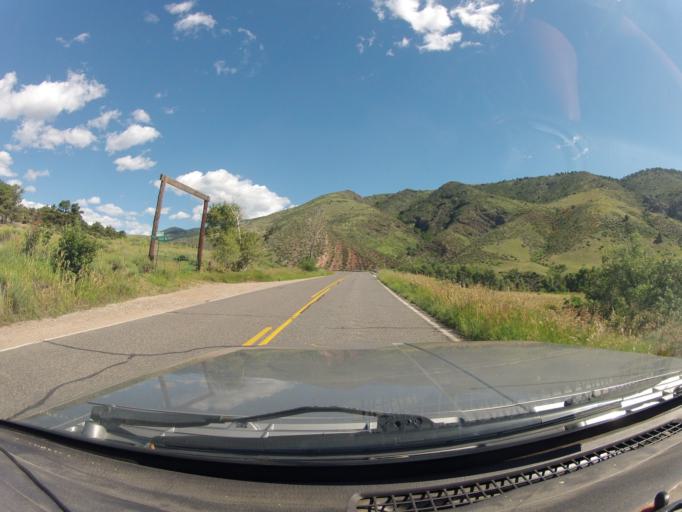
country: US
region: Colorado
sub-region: Larimer County
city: Laporte
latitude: 40.5072
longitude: -105.2295
